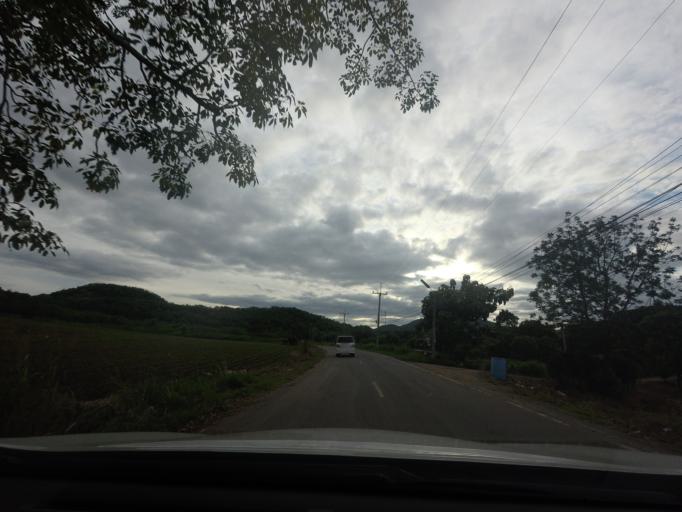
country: TH
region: Nakhon Ratchasima
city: Pak Chong
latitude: 14.6081
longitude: 101.4184
